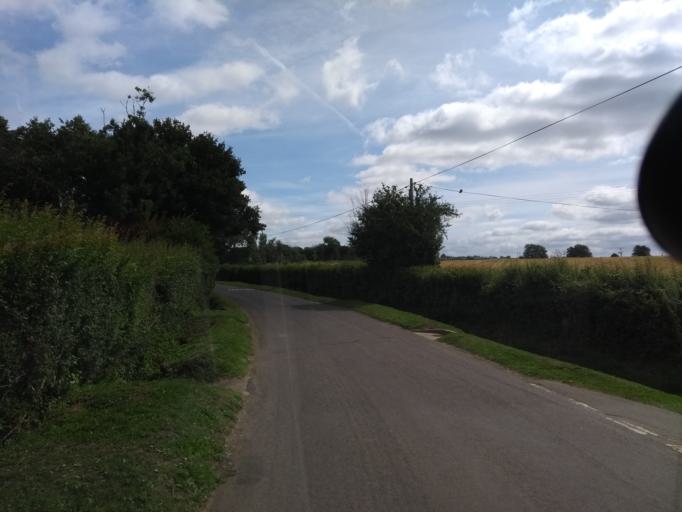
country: GB
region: England
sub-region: Somerset
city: South Petherton
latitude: 50.9277
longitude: -2.8457
